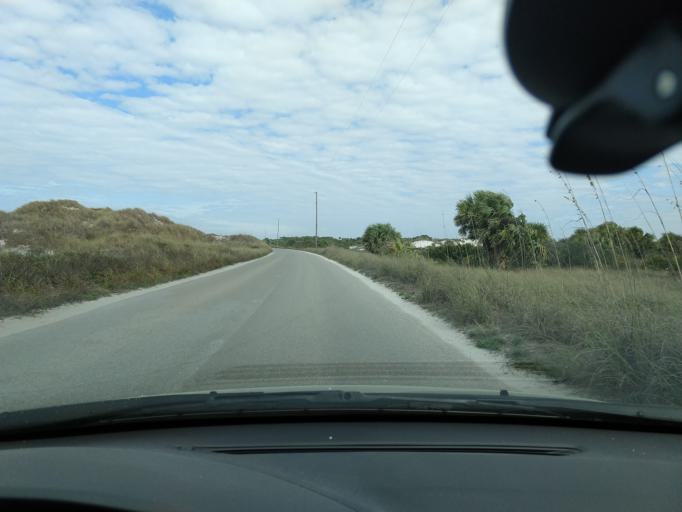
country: US
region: Florida
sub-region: Gulf County
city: Port Saint Joe
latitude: 29.7682
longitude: -85.4050
